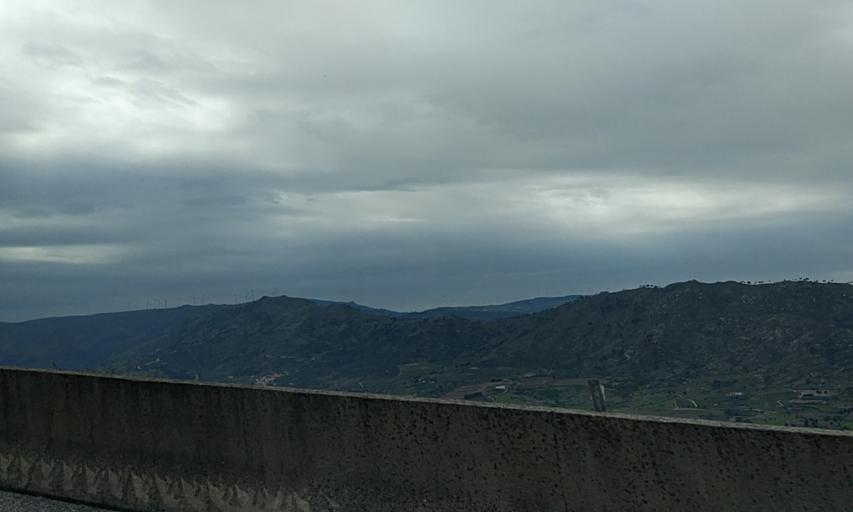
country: PT
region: Guarda
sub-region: Guarda
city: Guarda
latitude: 40.5985
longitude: -7.2755
